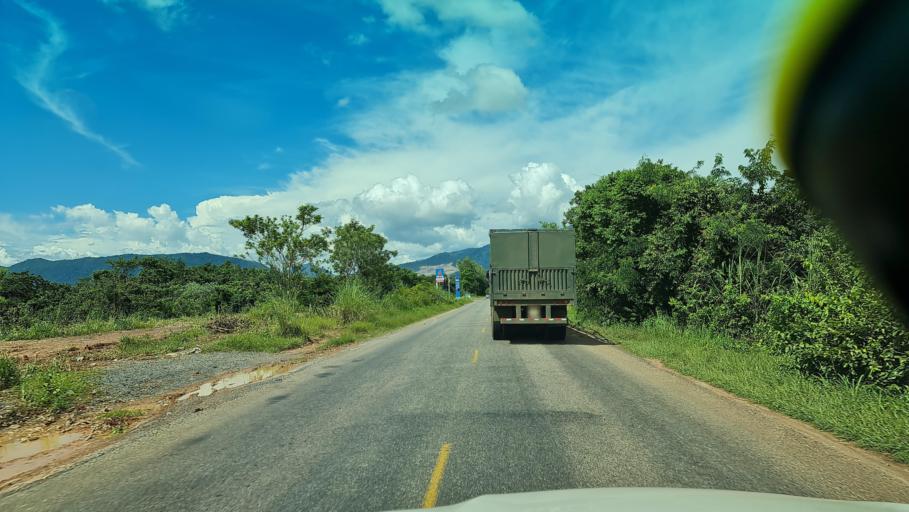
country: LA
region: Bolikhamxai
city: Pakkading
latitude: 18.2915
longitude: 104.0810
